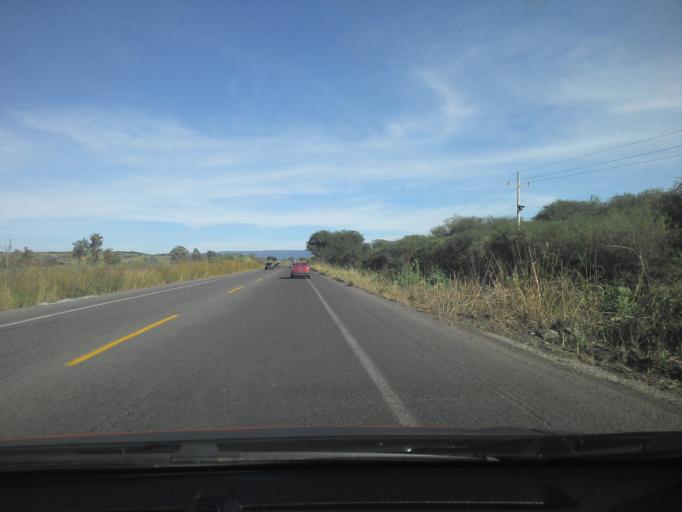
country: MX
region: Jalisco
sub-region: Teuchitlan
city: La Estanzuela
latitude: 20.6713
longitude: -103.8133
